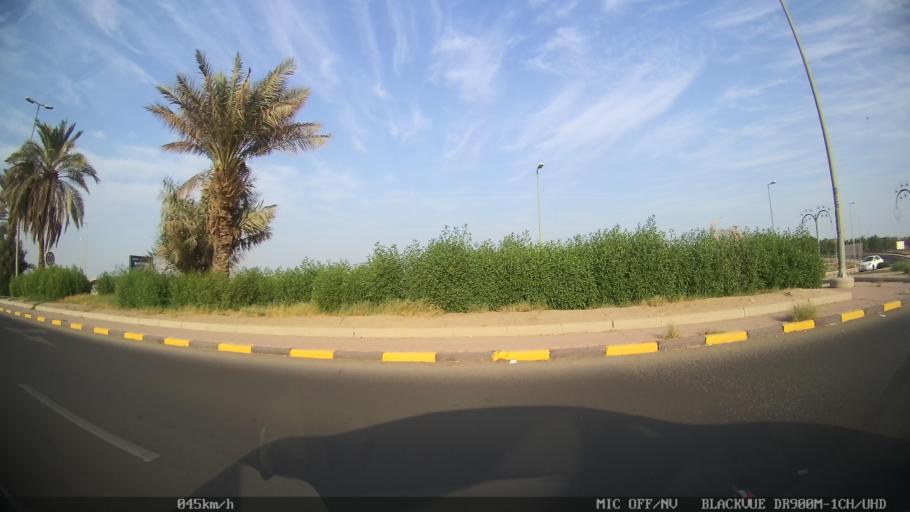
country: KW
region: Al Farwaniyah
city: Janub as Surrah
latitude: 29.2491
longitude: 47.9645
